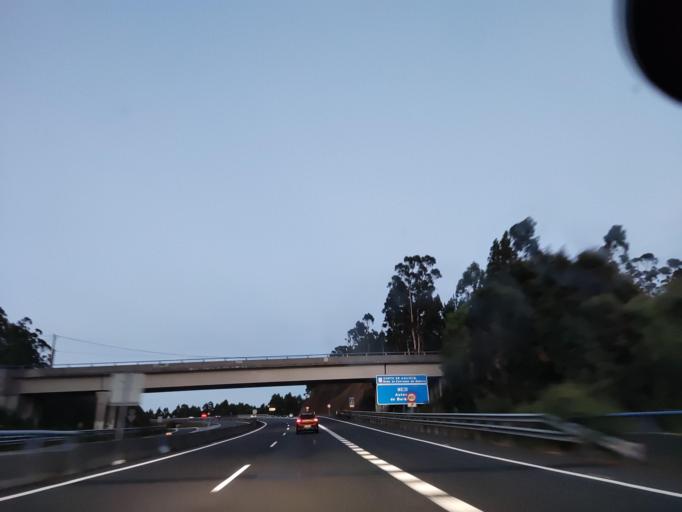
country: ES
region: Galicia
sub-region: Provincia da Coruna
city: Boiro
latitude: 42.6240
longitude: -8.9299
